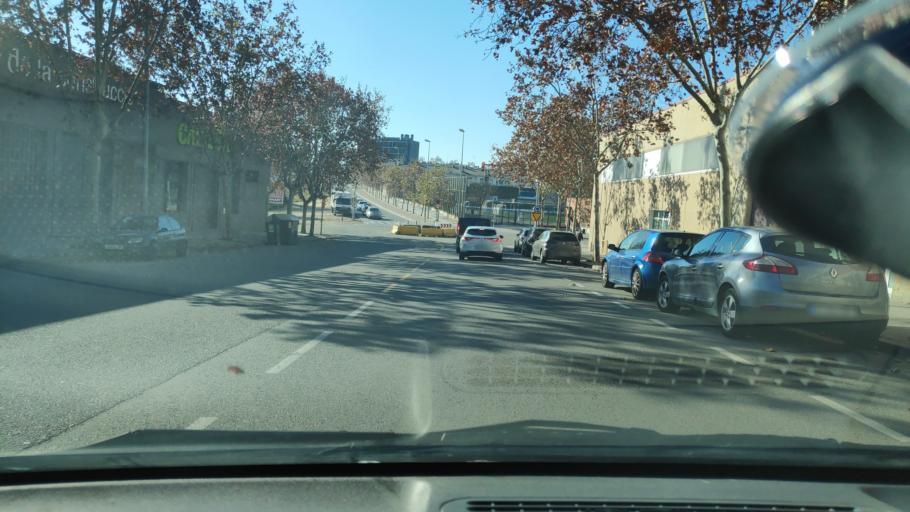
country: ES
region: Catalonia
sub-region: Provincia de Barcelona
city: Sant Quirze del Valles
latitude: 41.5414
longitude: 2.0929
